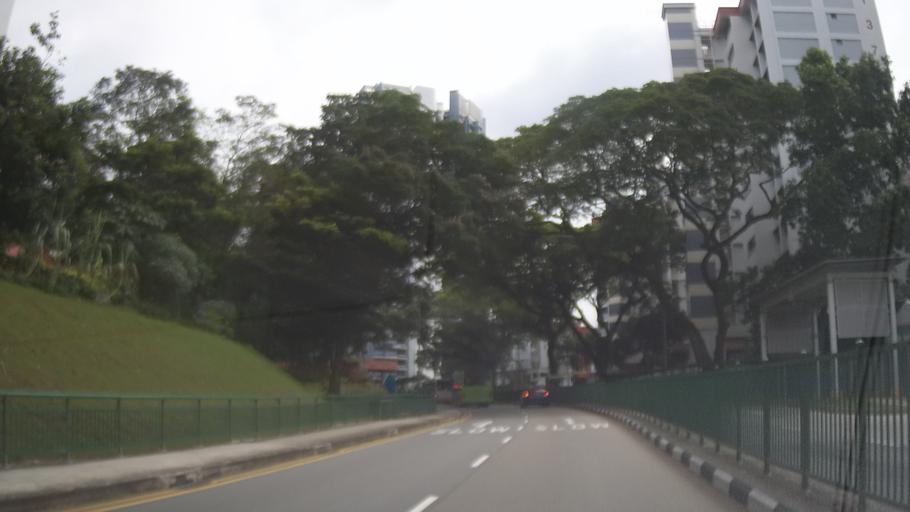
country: MY
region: Johor
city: Johor Bahru
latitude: 1.4387
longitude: 103.7758
